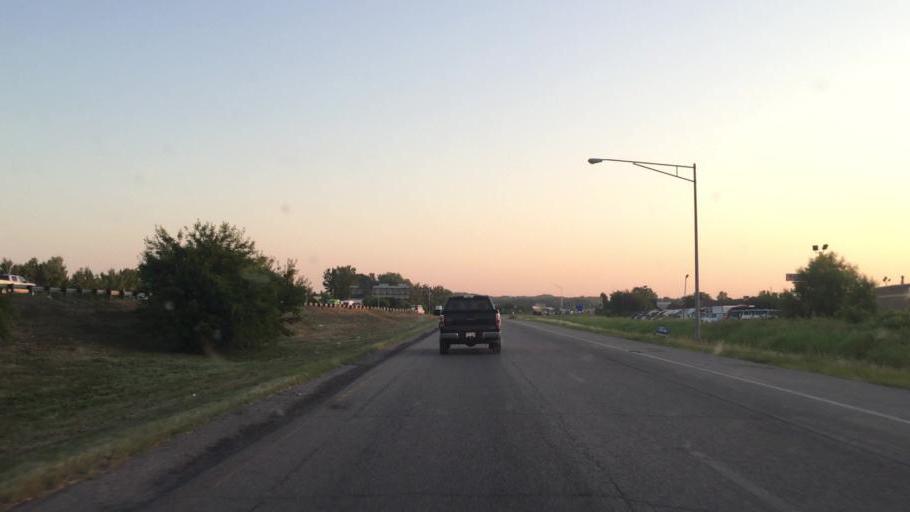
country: US
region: Missouri
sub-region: Jackson County
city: Sugar Creek
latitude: 39.1312
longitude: -94.4985
